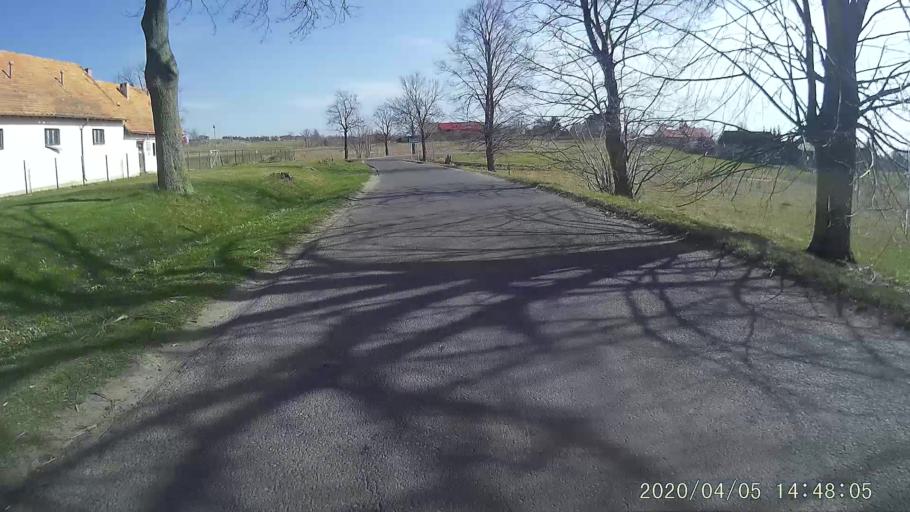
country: PL
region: Lower Silesian Voivodeship
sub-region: Powiat zgorzelecki
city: Sulikow
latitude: 51.0673
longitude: 15.1065
